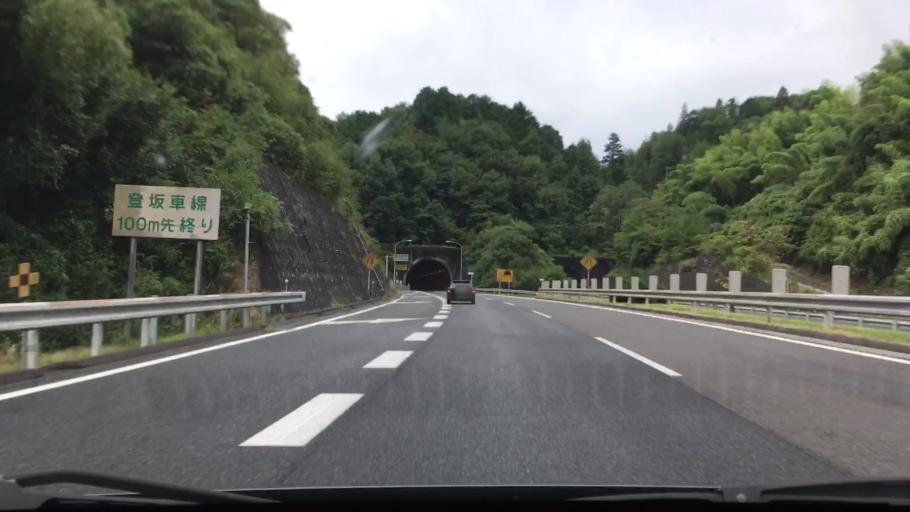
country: JP
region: Hiroshima
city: Hiroshima-shi
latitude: 34.5146
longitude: 132.4215
